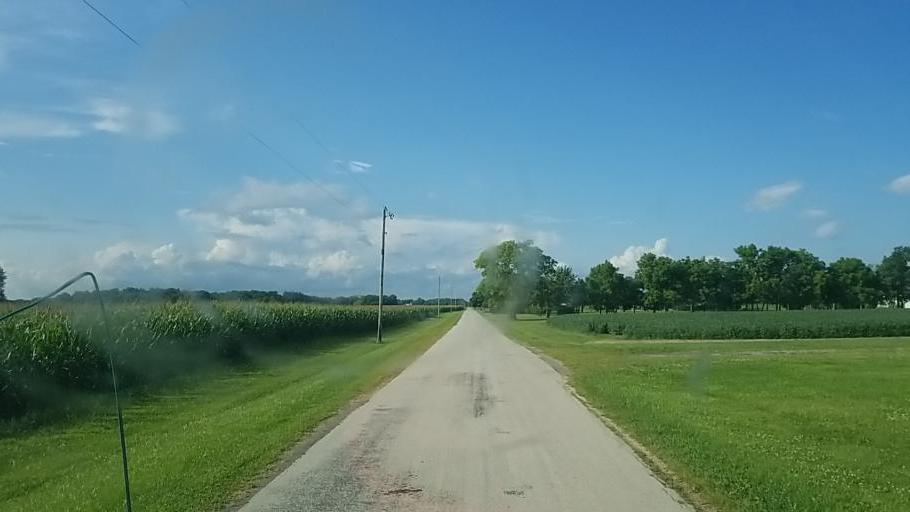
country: US
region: Ohio
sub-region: Wyandot County
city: Upper Sandusky
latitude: 40.7747
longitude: -83.3525
